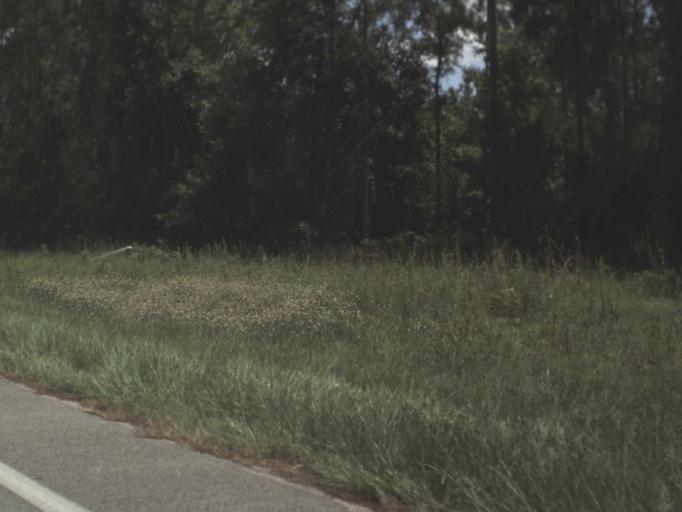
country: US
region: Florida
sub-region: Madison County
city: Madison
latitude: 30.5467
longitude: -83.6350
